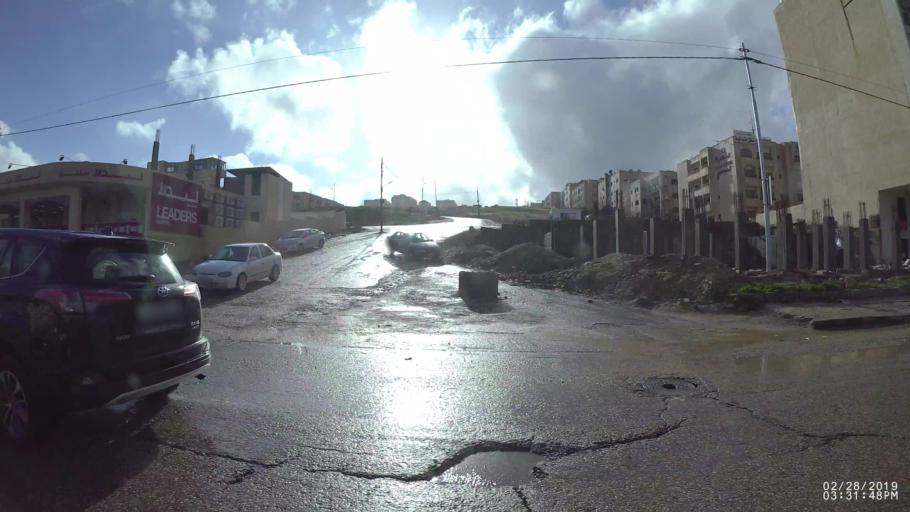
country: JO
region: Amman
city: Al Jubayhah
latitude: 32.0076
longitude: 35.8719
